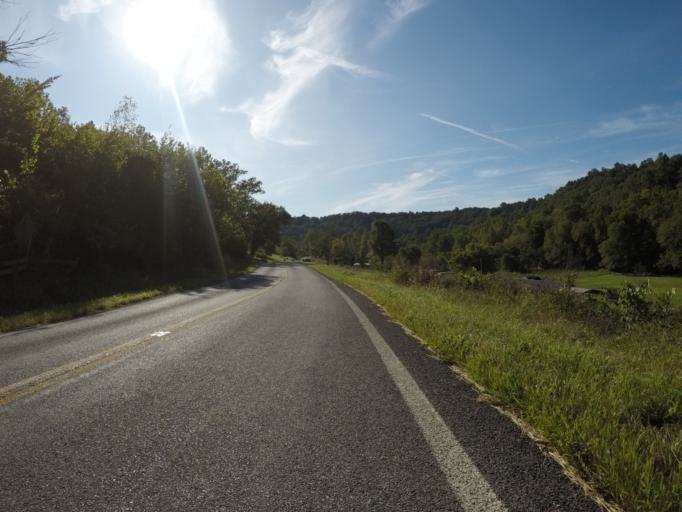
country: US
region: West Virginia
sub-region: Cabell County
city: Huntington
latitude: 38.4957
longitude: -82.5000
